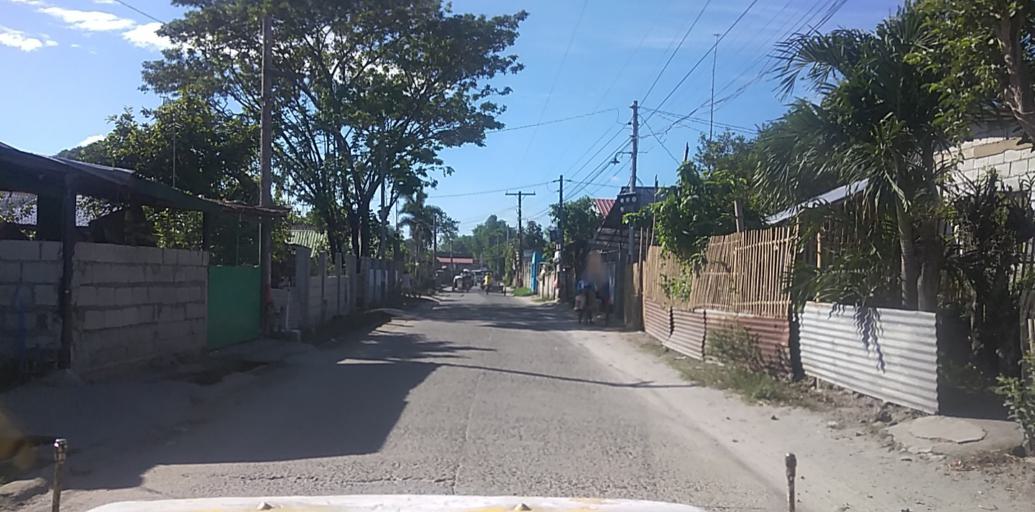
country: PH
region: Central Luzon
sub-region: Province of Pampanga
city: San Patricio
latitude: 15.0939
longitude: 120.7133
